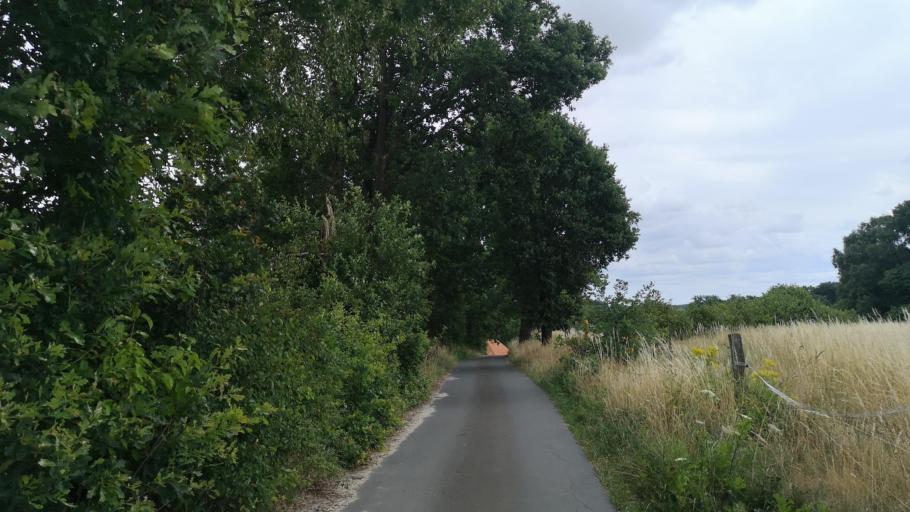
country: DE
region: Lower Saxony
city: Thomasburg
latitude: 53.2277
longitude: 10.6998
